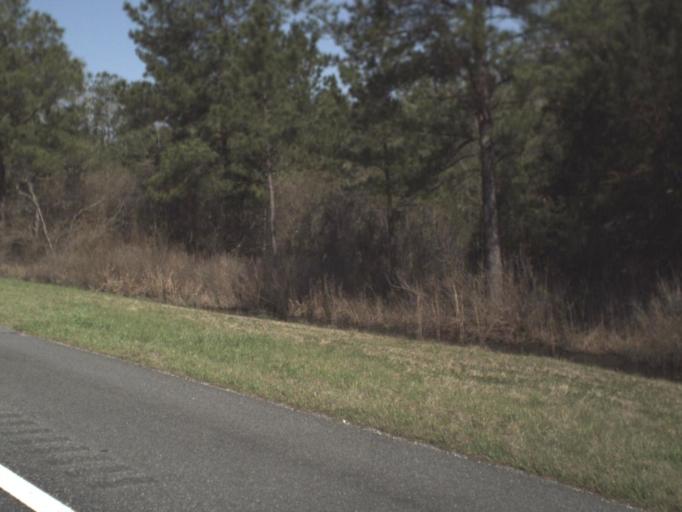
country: US
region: Florida
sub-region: Jackson County
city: Marianna
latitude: 30.7010
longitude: -85.1359
